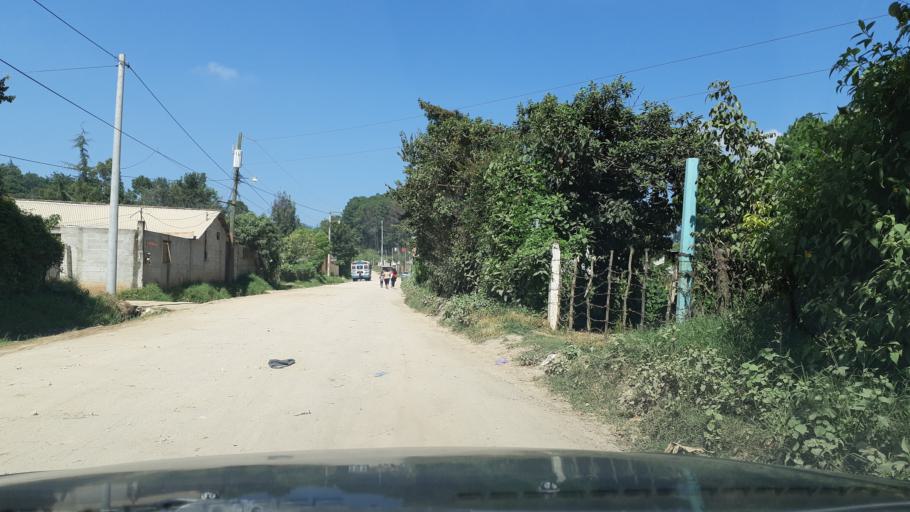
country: GT
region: Chimaltenango
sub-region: Municipio de Chimaltenango
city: Chimaltenango
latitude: 14.6690
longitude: -90.8370
